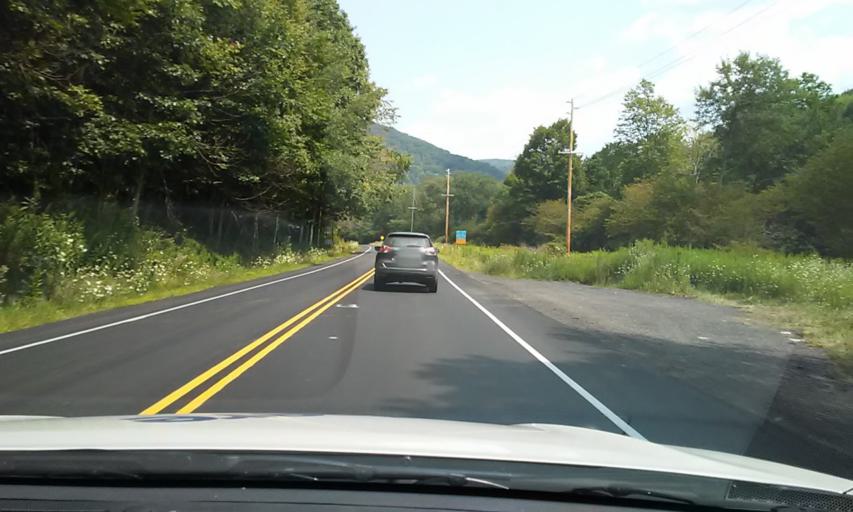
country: US
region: Pennsylvania
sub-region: Cameron County
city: Emporium
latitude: 41.4752
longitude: -78.3753
